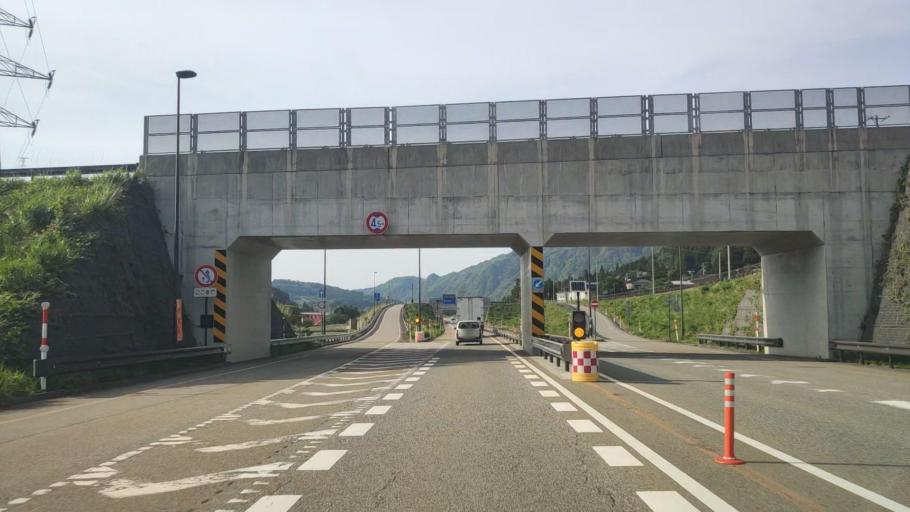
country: JP
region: Toyama
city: Yatsuomachi-higashikumisaka
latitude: 36.5193
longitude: 137.2311
